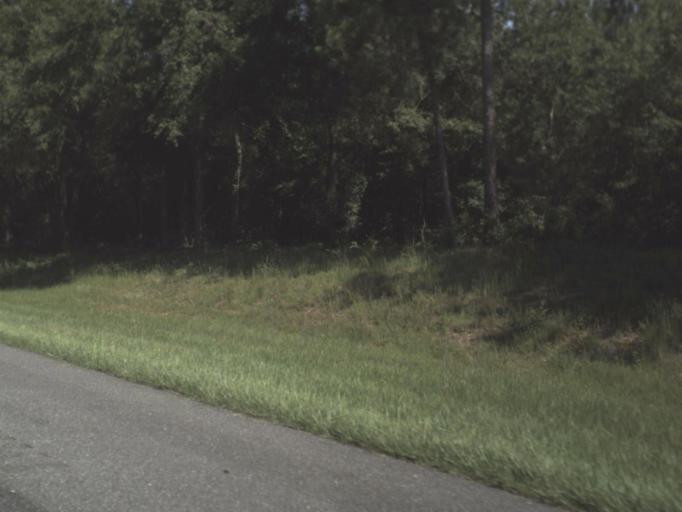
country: US
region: Florida
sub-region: Suwannee County
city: Live Oak
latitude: 30.3441
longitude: -83.1341
